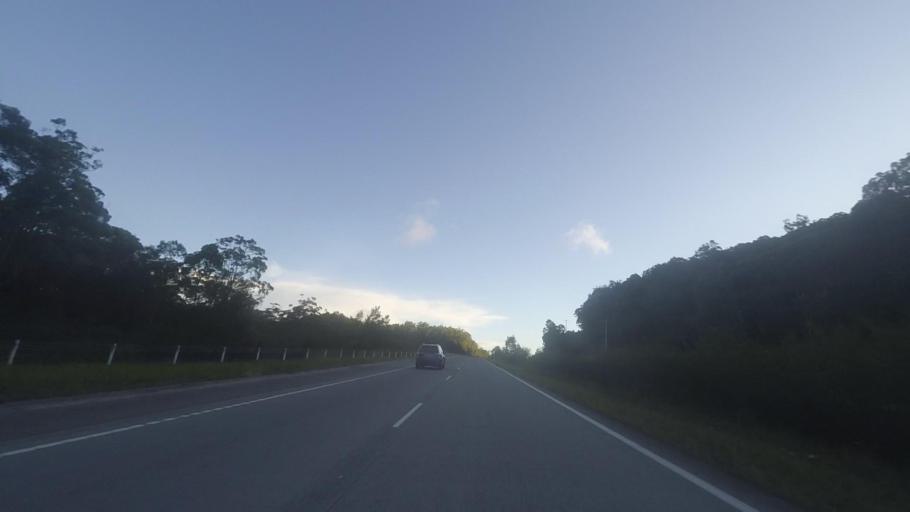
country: AU
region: New South Wales
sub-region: Great Lakes
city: Bulahdelah
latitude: -32.4708
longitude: 152.1955
